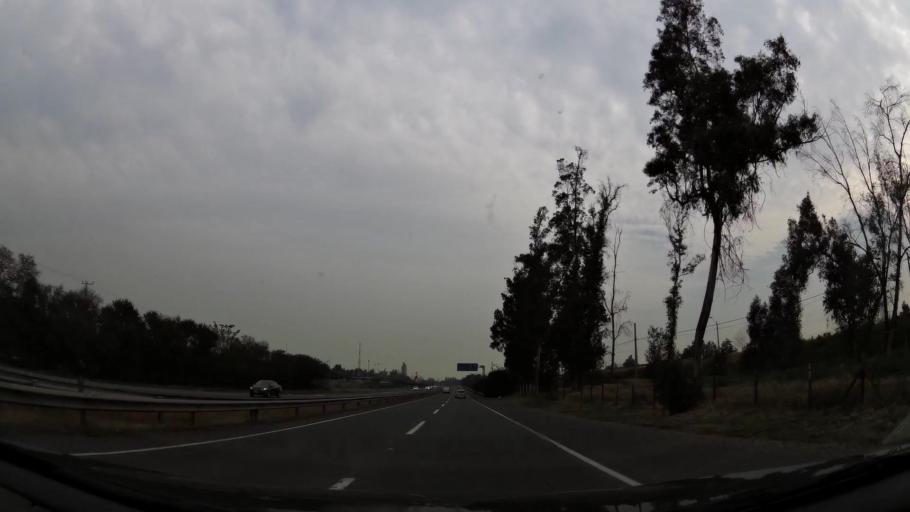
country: CL
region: Santiago Metropolitan
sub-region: Provincia de Chacabuco
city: Chicureo Abajo
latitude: -33.2313
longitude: -70.6904
